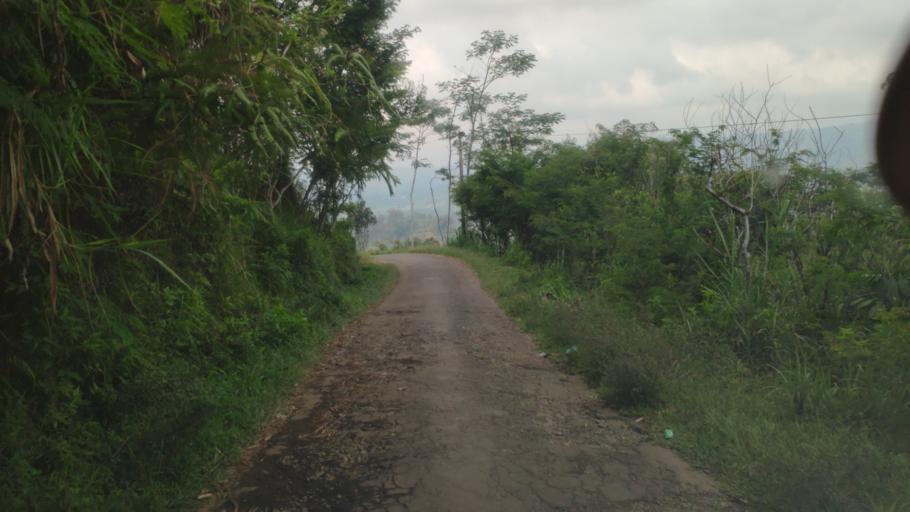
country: ID
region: Central Java
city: Wonosobo
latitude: -7.2687
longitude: 109.8109
